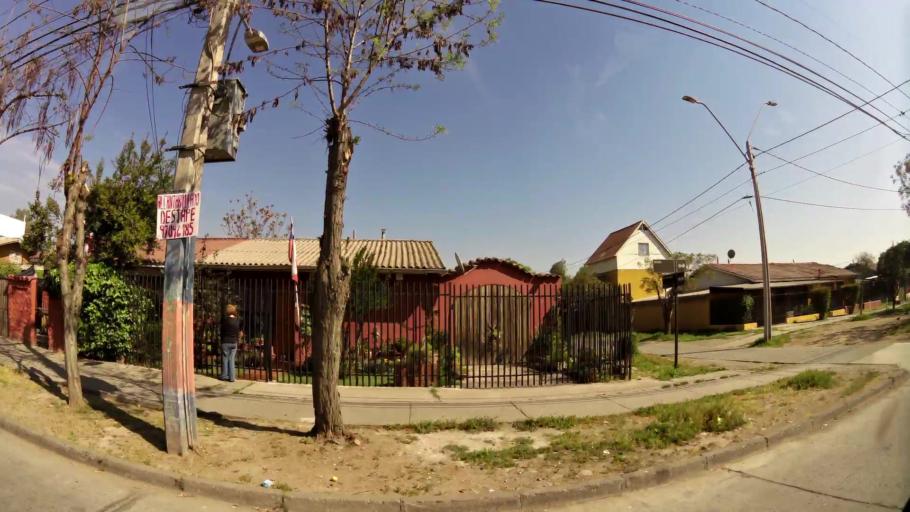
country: CL
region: Santiago Metropolitan
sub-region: Provincia de Maipo
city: San Bernardo
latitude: -33.5900
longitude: -70.7001
